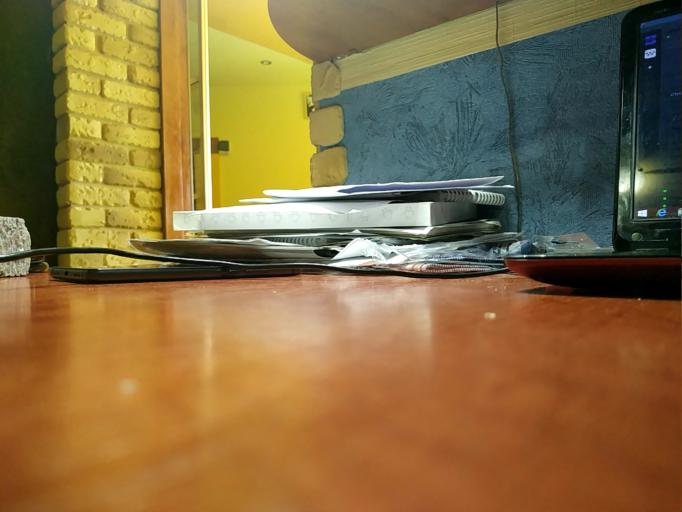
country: RU
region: Vologda
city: Khokhlovo
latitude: 59.4421
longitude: 37.3362
